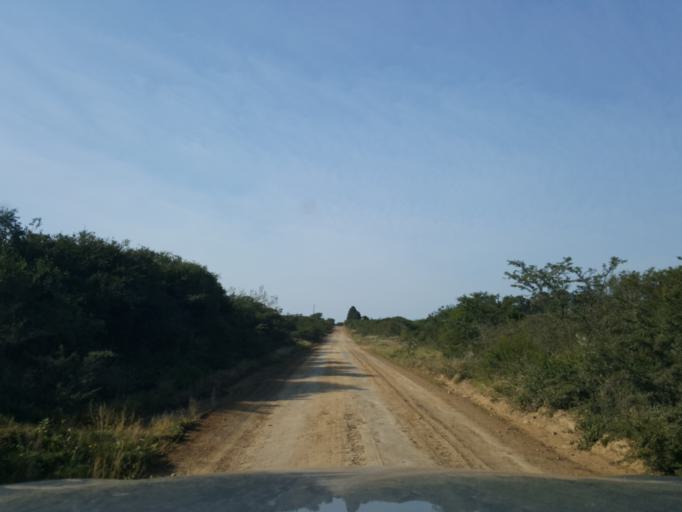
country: ZA
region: Eastern Cape
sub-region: Cacadu District Municipality
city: Grahamstown
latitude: -33.4120
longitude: 26.3092
